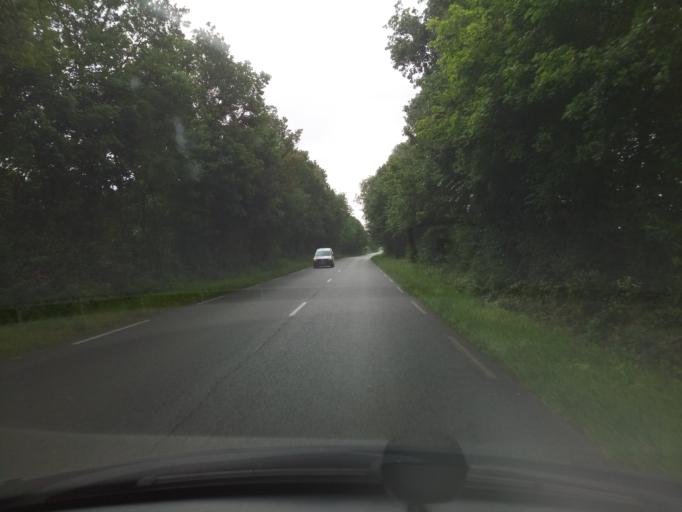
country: FR
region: Poitou-Charentes
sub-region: Departement de la Charente-Maritime
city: Courcon
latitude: 46.1809
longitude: -0.8523
